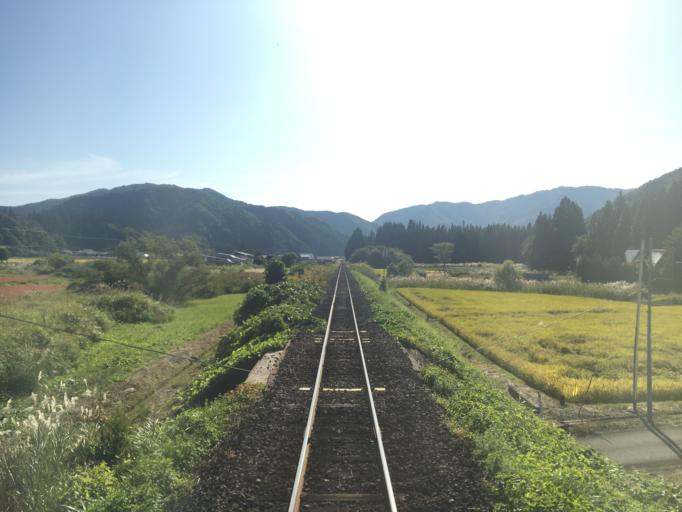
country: JP
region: Akita
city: Kakunodatemachi
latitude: 39.7424
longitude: 140.5884
